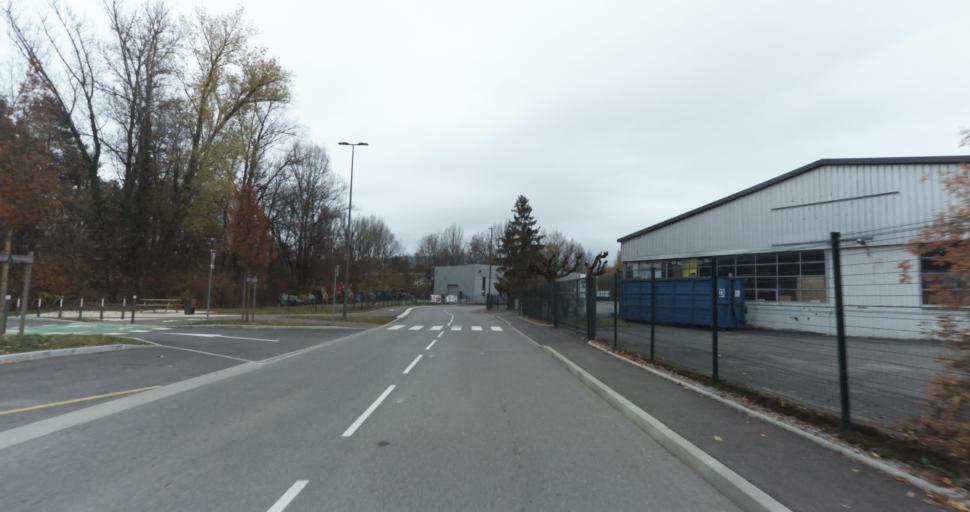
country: FR
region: Rhone-Alpes
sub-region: Departement de la Haute-Savoie
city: Meythet
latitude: 45.9160
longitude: 6.1058
